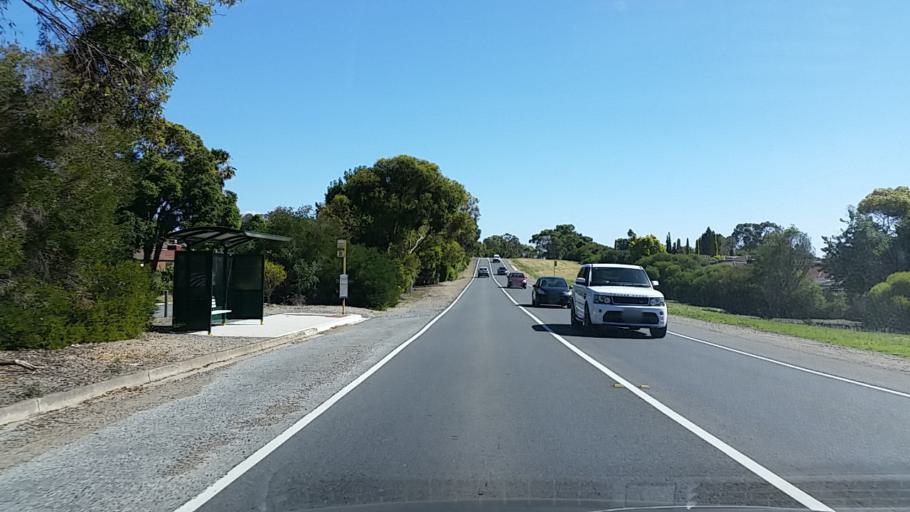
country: AU
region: South Australia
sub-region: Tea Tree Gully
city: Golden Grove
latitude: -34.7998
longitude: 138.7062
